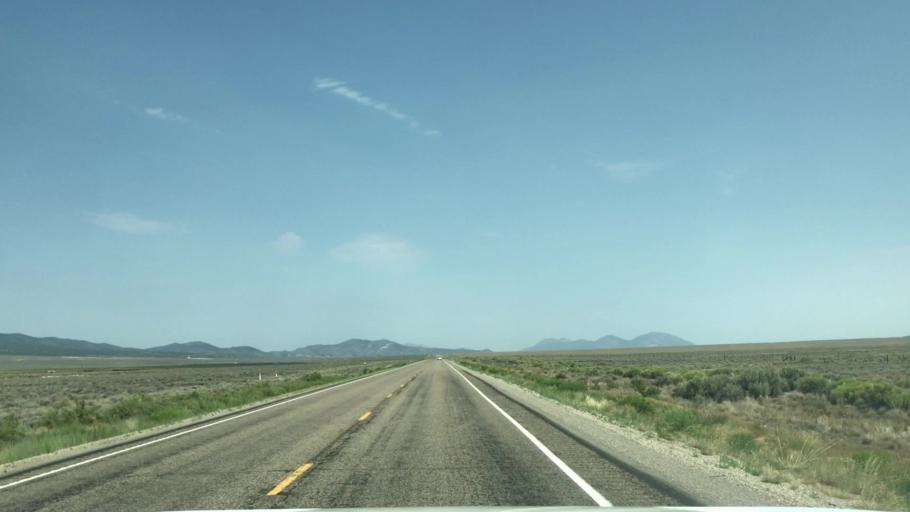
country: US
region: Nevada
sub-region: White Pine County
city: Ely
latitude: 39.1230
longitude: -114.7764
